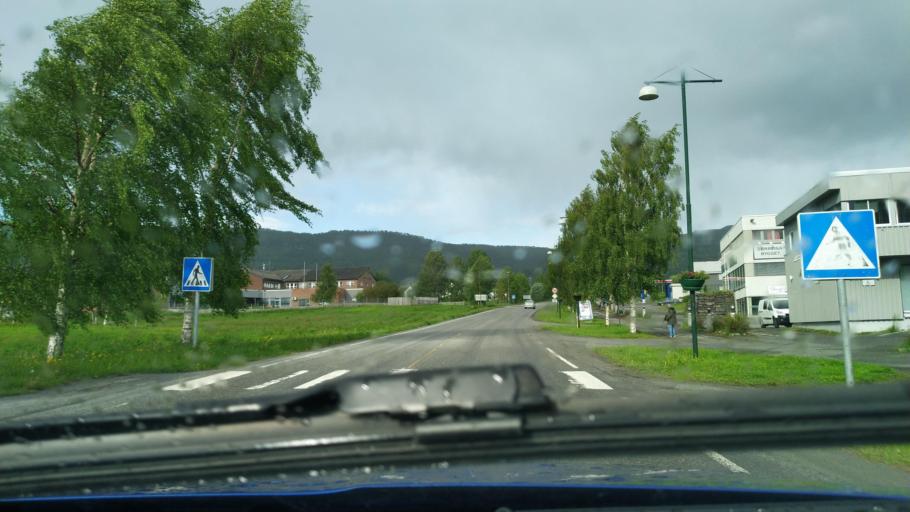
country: NO
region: Troms
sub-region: Sorreisa
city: Sorreisa
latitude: 69.1454
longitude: 18.1532
